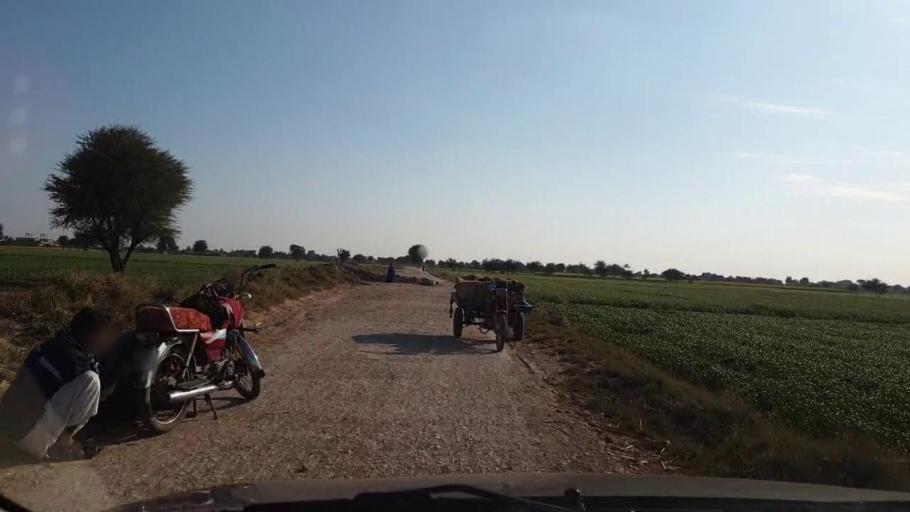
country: PK
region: Sindh
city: Jhol
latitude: 25.9679
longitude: 68.8394
